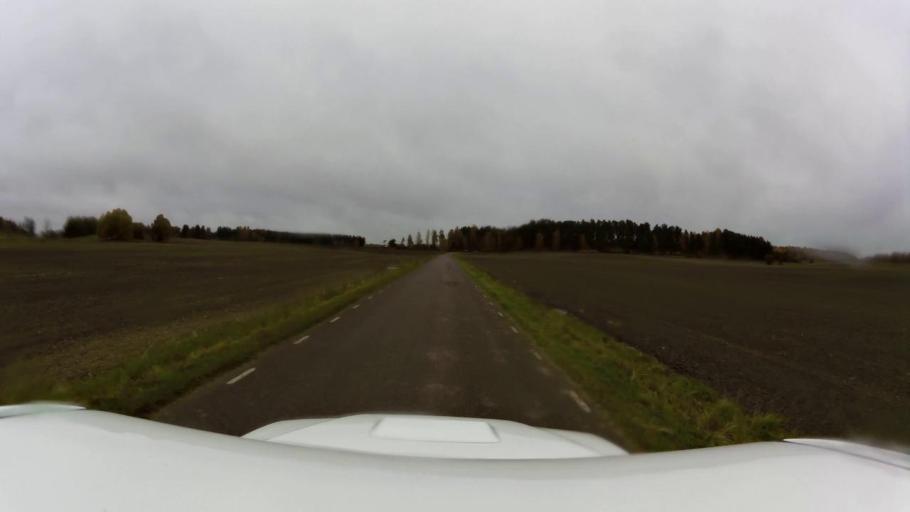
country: SE
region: OEstergoetland
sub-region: Norrkopings Kommun
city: Kimstad
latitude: 58.3948
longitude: 15.9504
